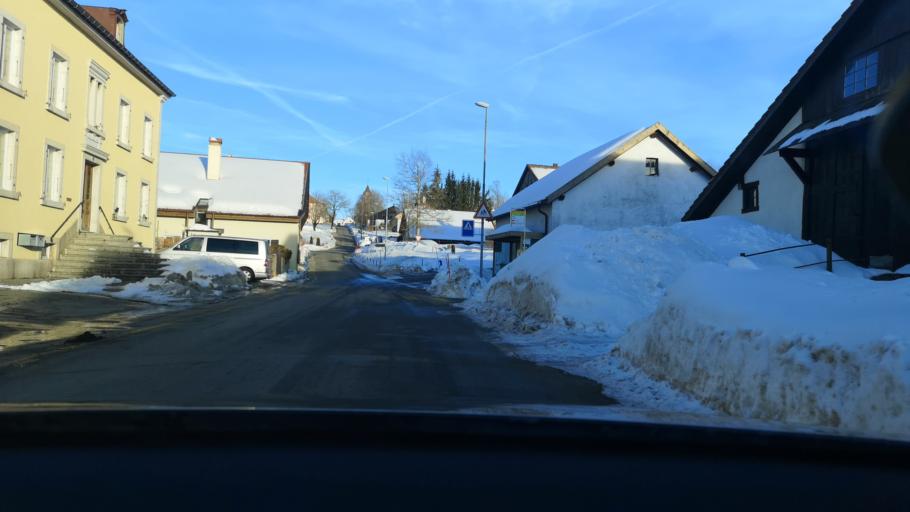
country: CH
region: Neuchatel
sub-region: Val-de-Travers District
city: Fleurier
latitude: 46.9163
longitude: 6.5155
